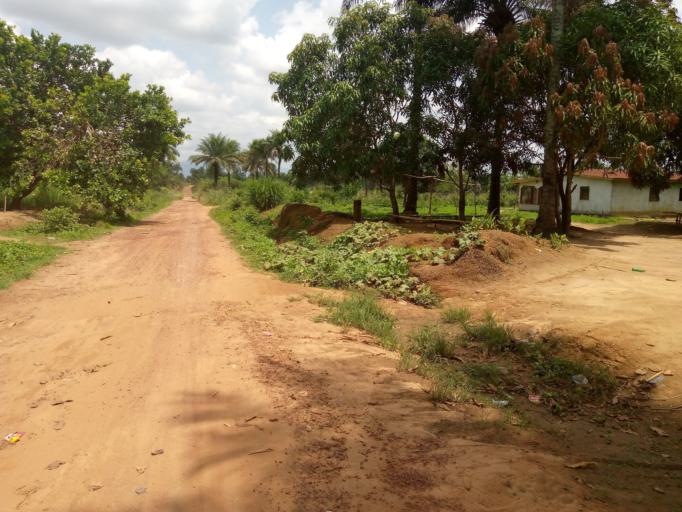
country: SL
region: Western Area
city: Waterloo
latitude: 8.3791
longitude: -12.9728
